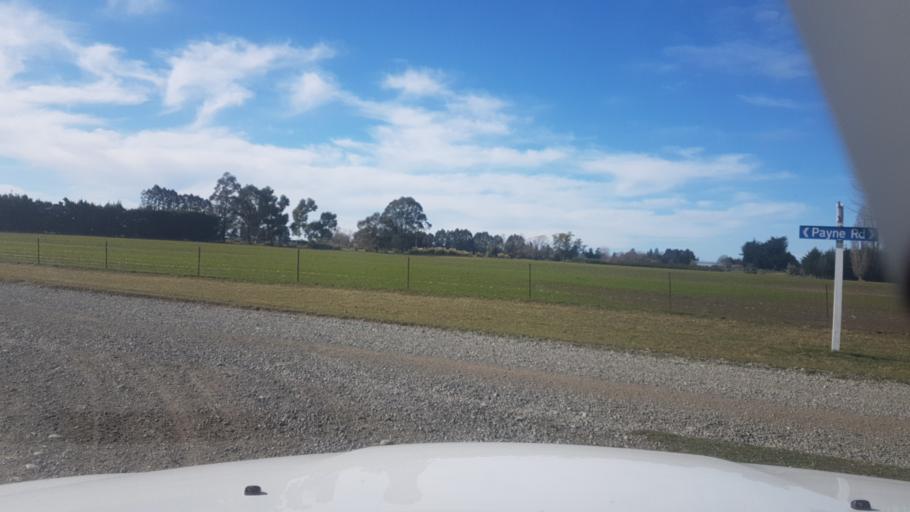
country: NZ
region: Canterbury
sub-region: Timaru District
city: Pleasant Point
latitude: -44.1373
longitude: 171.2768
